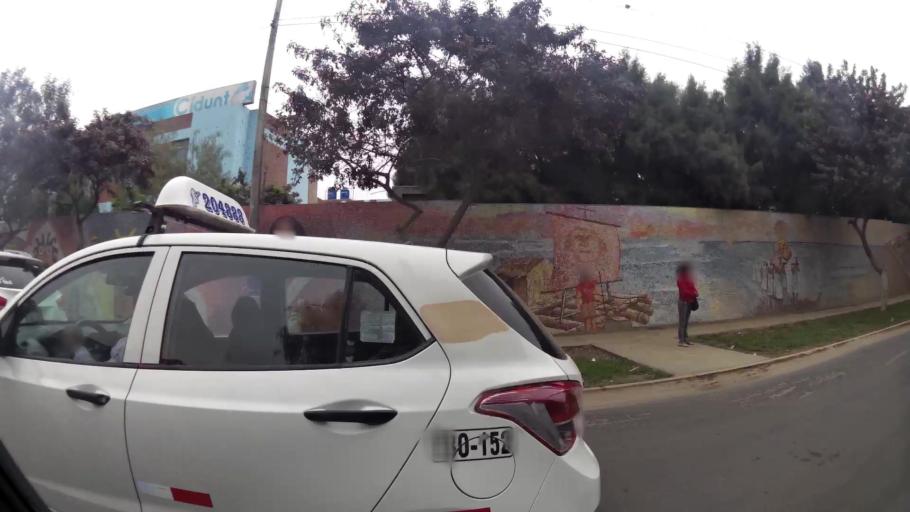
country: PE
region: La Libertad
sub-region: Provincia de Trujillo
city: Trujillo
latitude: -8.1111
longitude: -79.0365
